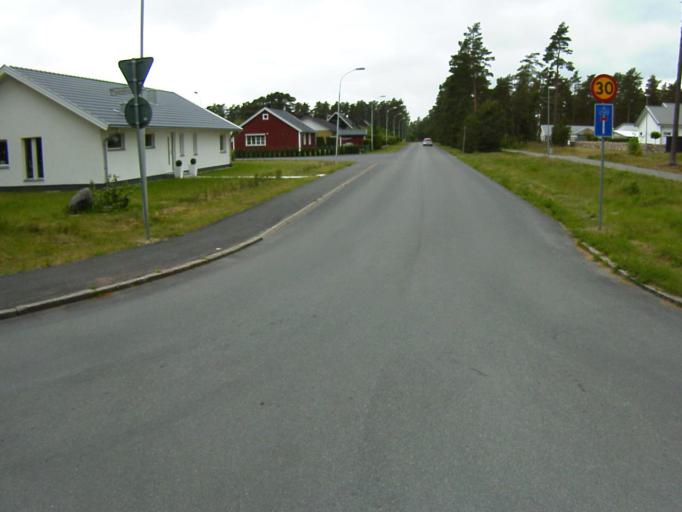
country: SE
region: Skane
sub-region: Kristianstads Kommun
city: Ahus
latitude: 55.9432
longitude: 14.2986
